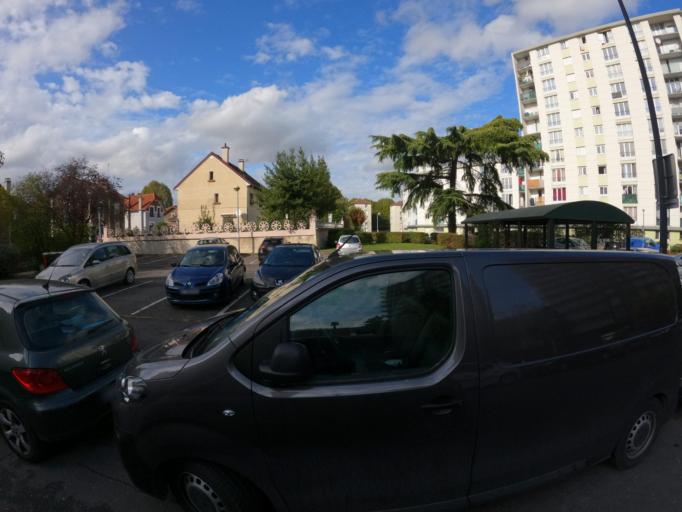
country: FR
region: Ile-de-France
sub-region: Departement de Seine-et-Marne
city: Chelles
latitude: 48.8796
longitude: 2.5918
